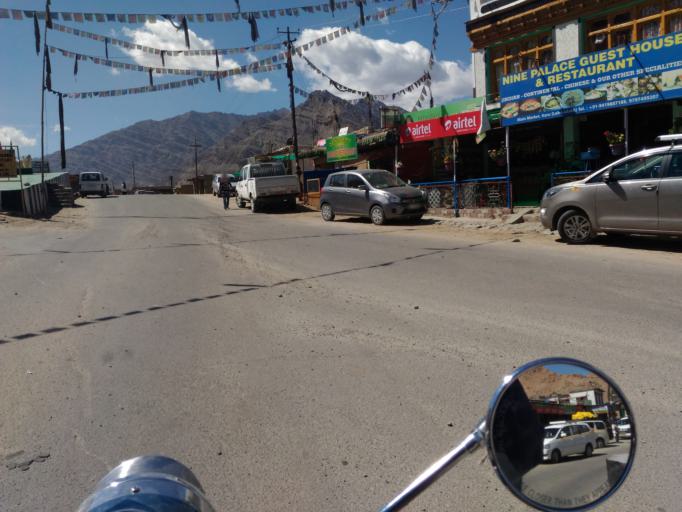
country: IN
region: Kashmir
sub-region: Ladakh
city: Leh
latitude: 33.9247
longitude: 77.7352
